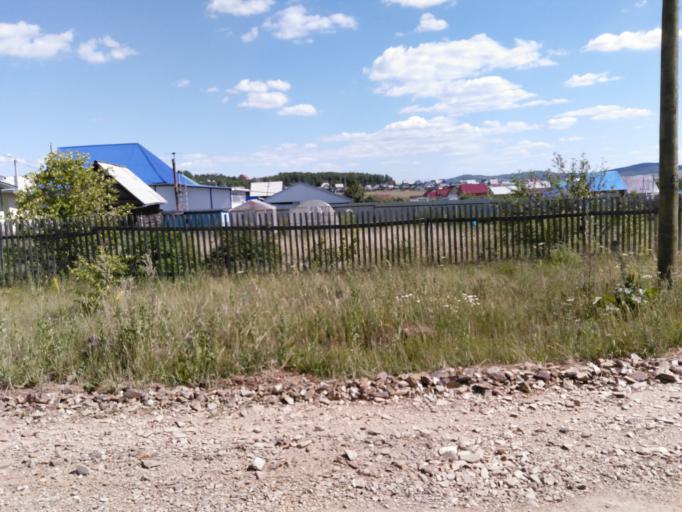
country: RU
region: Bashkortostan
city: Uchaly
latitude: 54.2908
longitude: 59.3605
